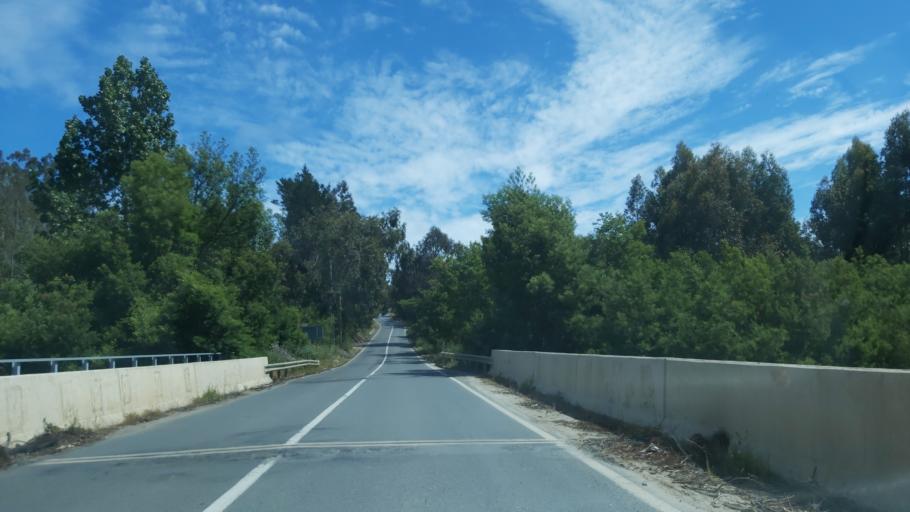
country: CL
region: Maule
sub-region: Provincia de Talca
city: Constitucion
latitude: -35.5671
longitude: -72.6024
